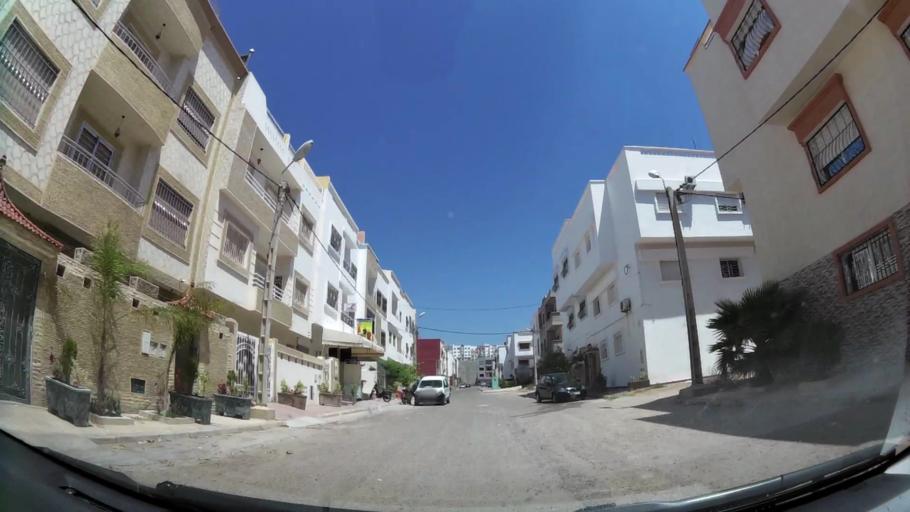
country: MA
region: Oued ed Dahab-Lagouira
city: Dakhla
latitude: 30.4307
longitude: -9.5628
